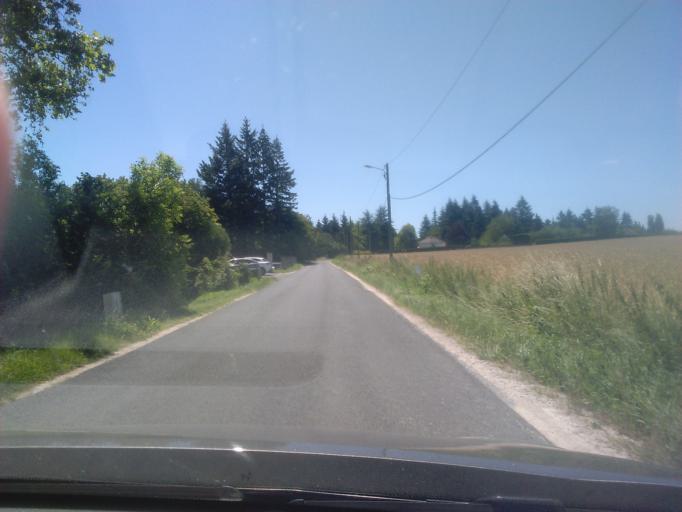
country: FR
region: Centre
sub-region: Departement du Loir-et-Cher
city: Saint-Sulpice-de-Pommeray
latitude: 47.6064
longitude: 1.2322
